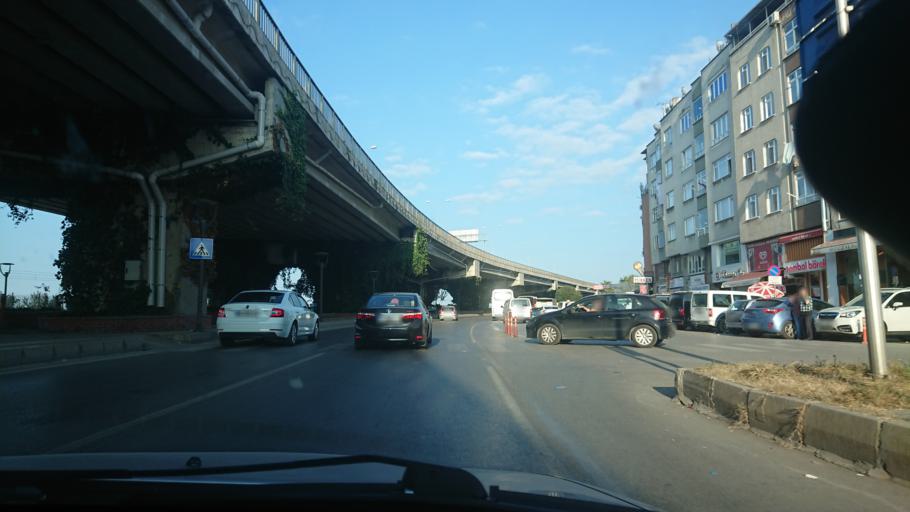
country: TR
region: Samsun
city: Samsun
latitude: 41.2722
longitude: 36.3663
